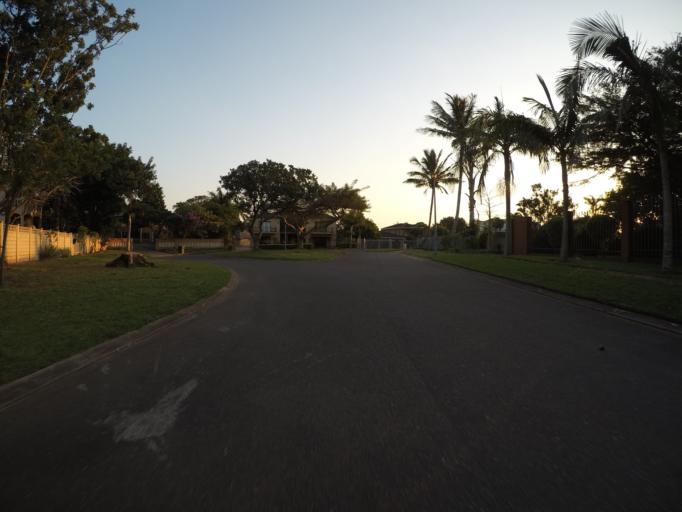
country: ZA
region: KwaZulu-Natal
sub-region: uThungulu District Municipality
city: Richards Bay
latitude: -28.7648
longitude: 32.1150
